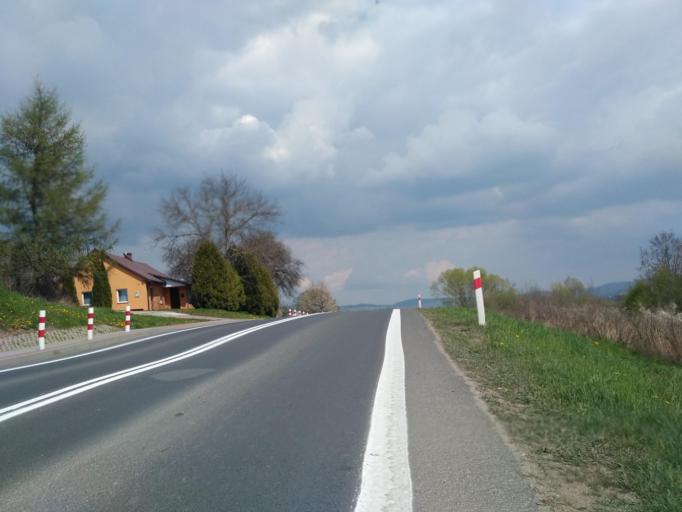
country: PL
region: Subcarpathian Voivodeship
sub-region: Powiat sanocki
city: Nowosielce-Gniewosz
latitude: 49.5603
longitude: 22.1142
